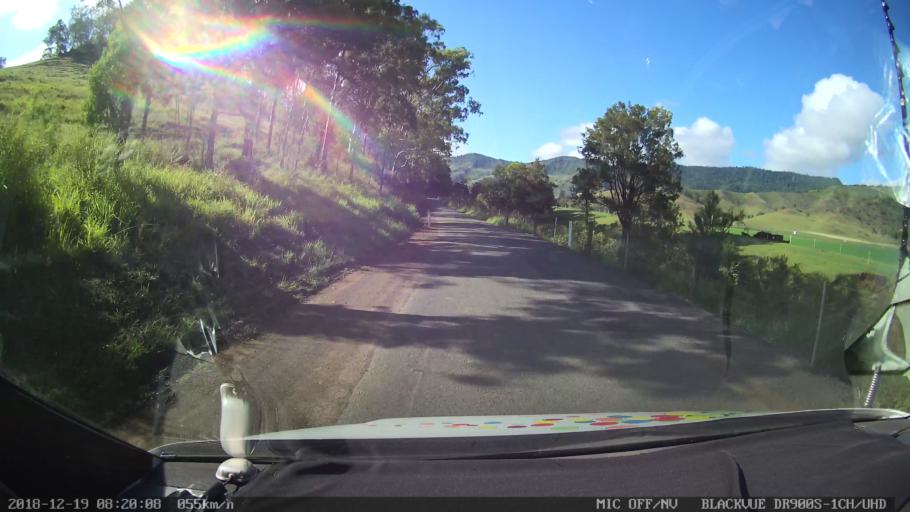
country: AU
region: New South Wales
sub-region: Kyogle
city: Kyogle
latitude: -28.2879
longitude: 152.9099
